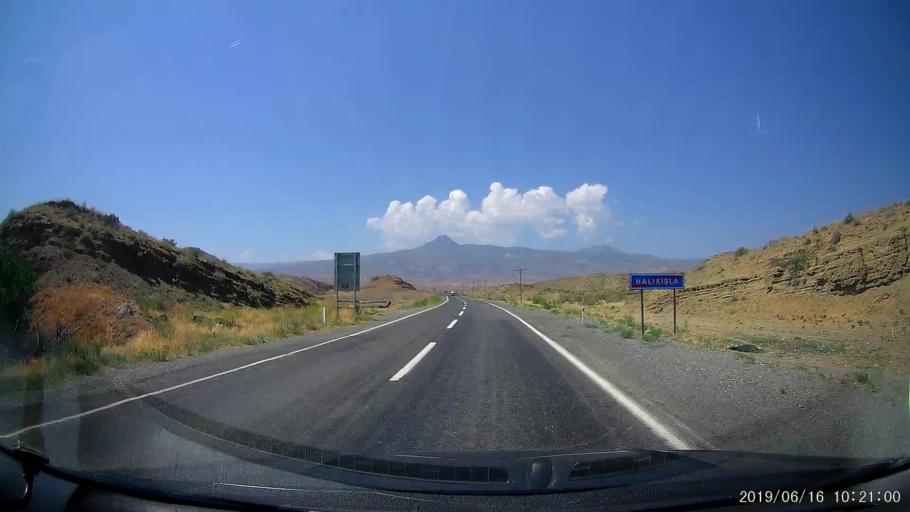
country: TR
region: Igdir
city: Tuzluca
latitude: 40.1422
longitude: 43.6415
